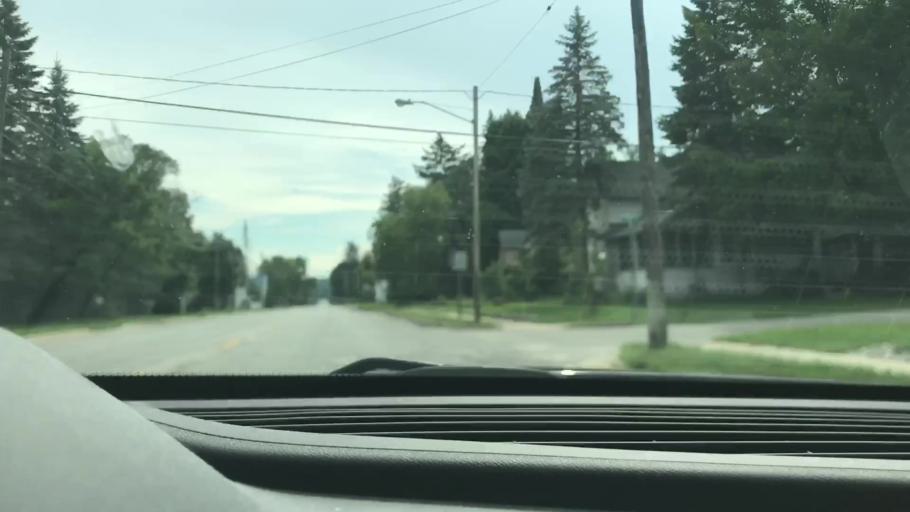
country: US
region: Michigan
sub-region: Antrim County
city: Bellaire
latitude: 45.0674
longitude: -85.2642
